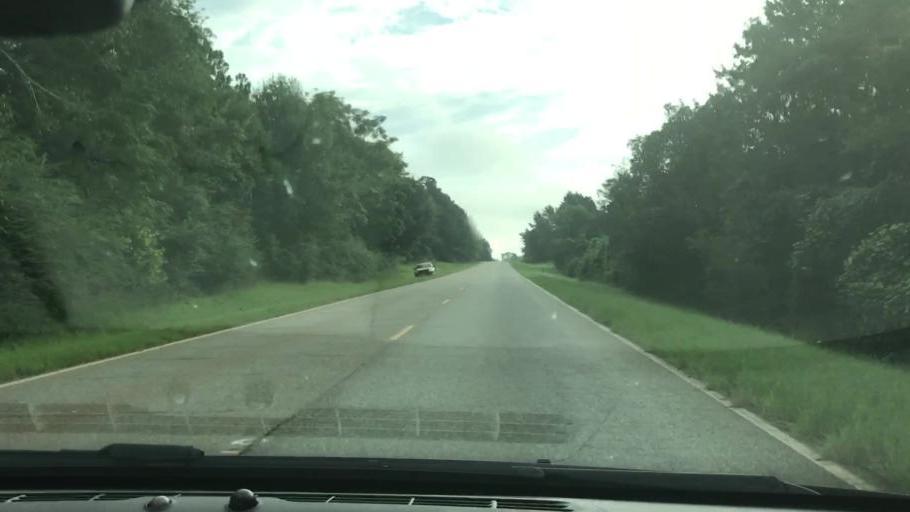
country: US
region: Georgia
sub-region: Quitman County
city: Georgetown
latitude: 31.8992
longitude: -85.0488
